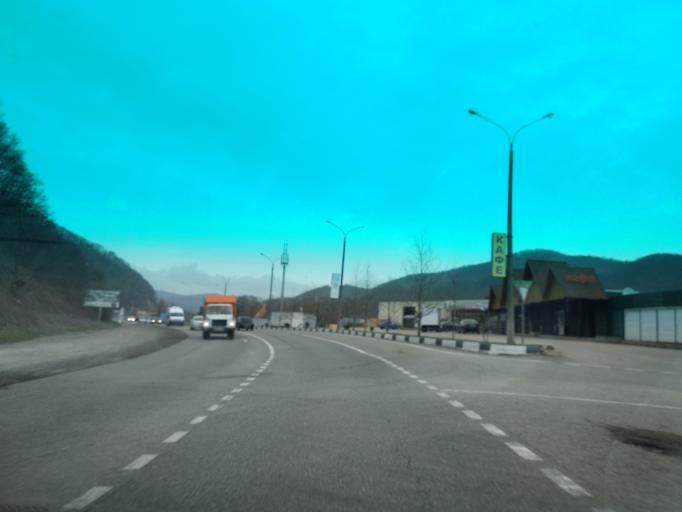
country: RU
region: Krasnodarskiy
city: Ol'ginka
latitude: 44.2135
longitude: 38.8947
